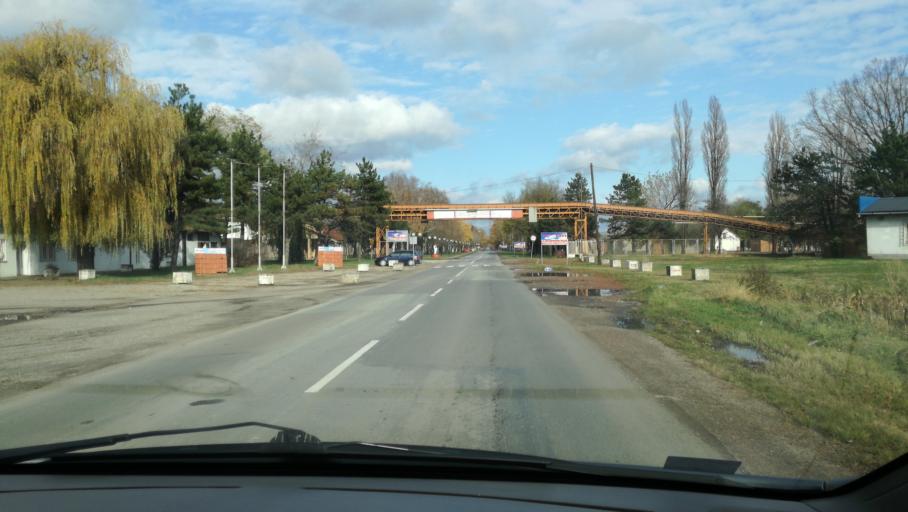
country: RS
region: Autonomna Pokrajina Vojvodina
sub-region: Severnobanatski Okrug
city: Kikinda
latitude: 45.8070
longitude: 20.4453
